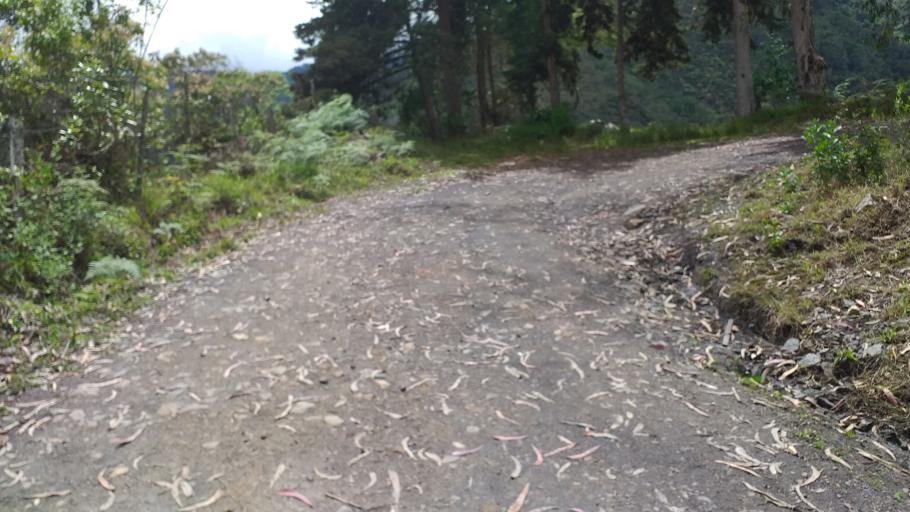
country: CO
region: Cundinamarca
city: Tenza
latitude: 5.1229
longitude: -73.4606
